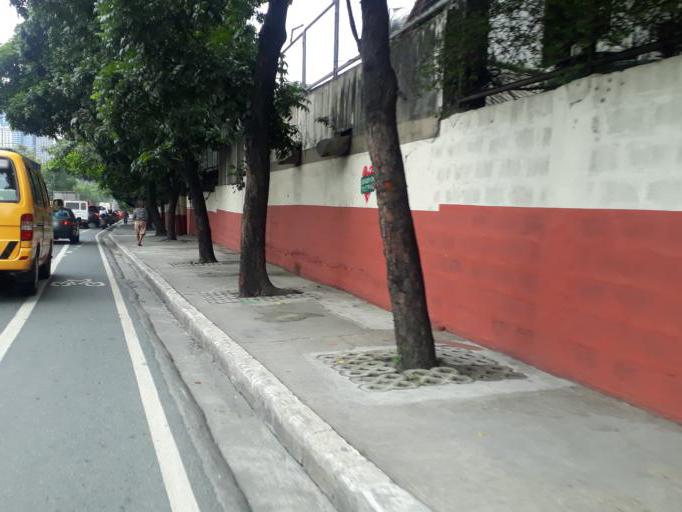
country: PH
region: Metro Manila
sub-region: Pasig
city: Pasig City
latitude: 14.5897
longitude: 121.0762
